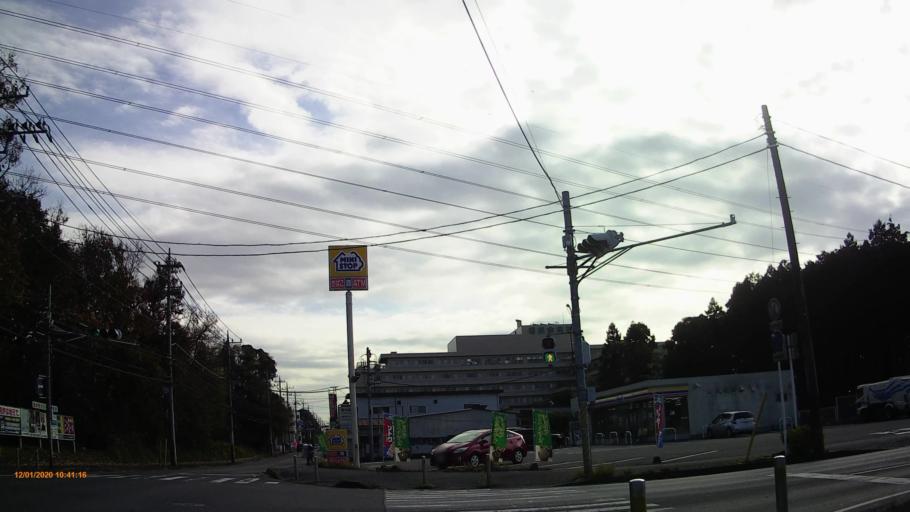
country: JP
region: Chiba
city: Yotsukaido
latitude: 35.6302
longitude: 140.1854
